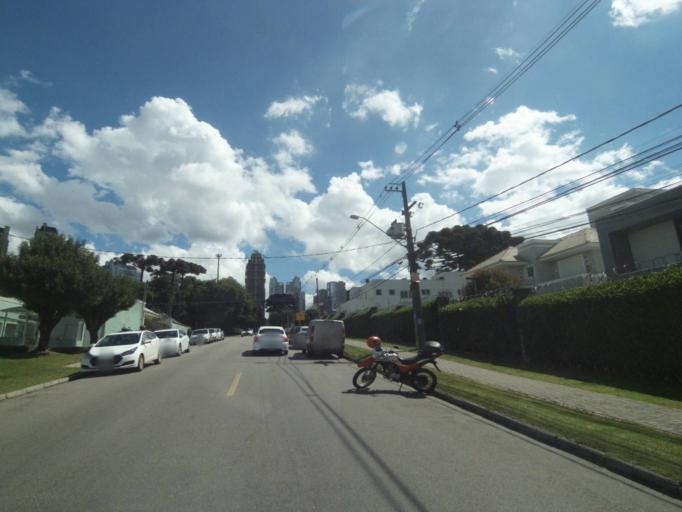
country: BR
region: Parana
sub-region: Curitiba
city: Curitiba
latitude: -25.4339
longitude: -49.3349
